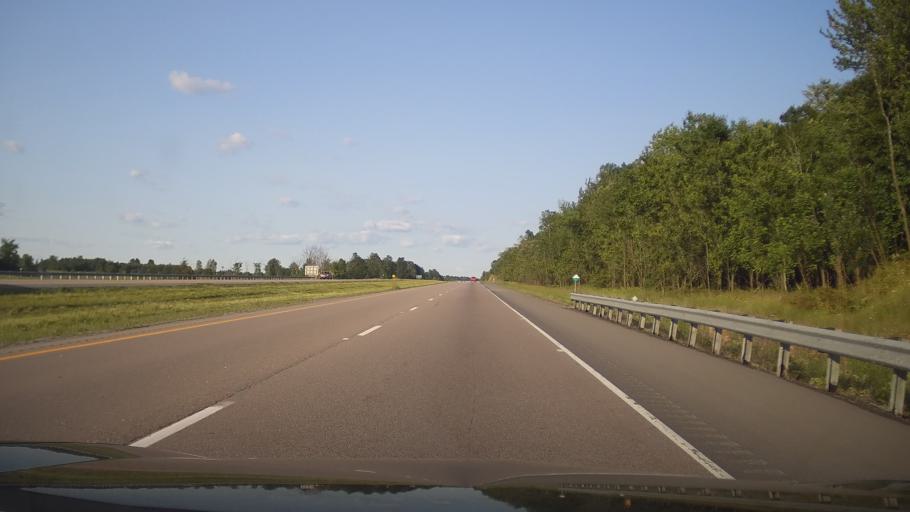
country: CA
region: Ontario
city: Gananoque
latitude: 44.3654
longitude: -76.0691
